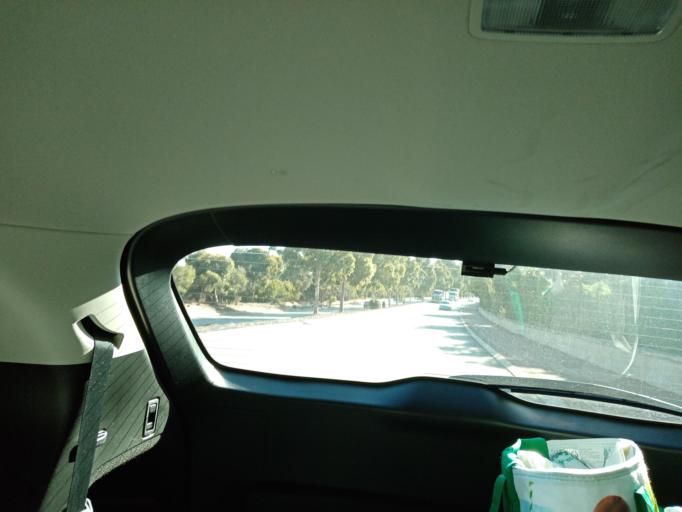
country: AU
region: Western Australia
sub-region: City of Cockburn
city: Yangebup
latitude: -32.1281
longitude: 115.8128
